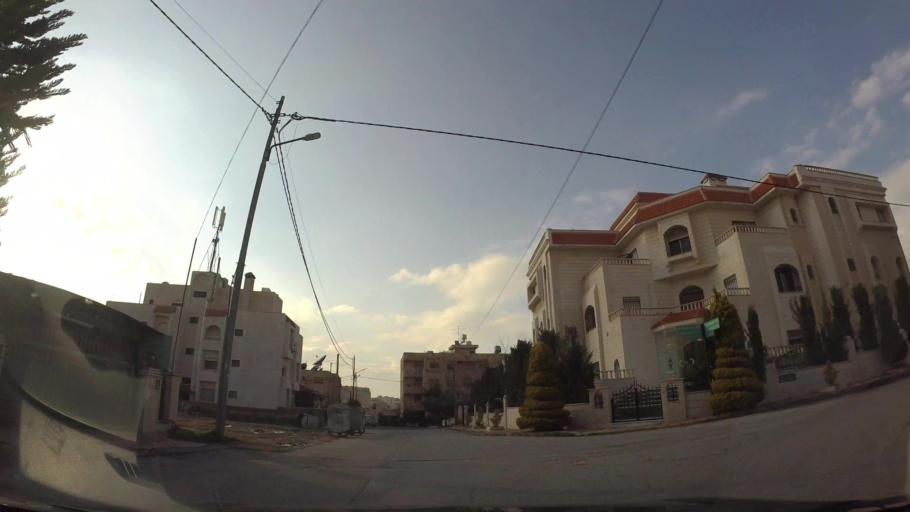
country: JO
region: Amman
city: Al Jubayhah
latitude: 31.9838
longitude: 35.8708
